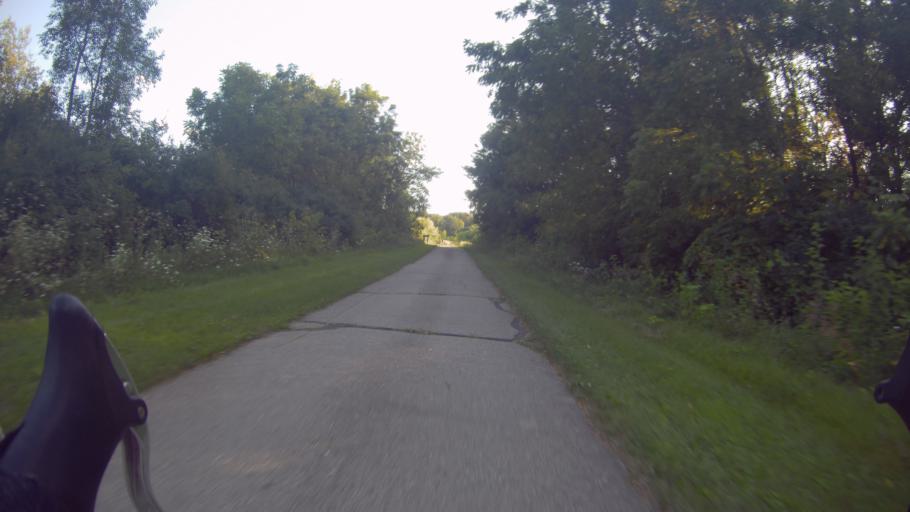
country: US
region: Wisconsin
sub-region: Dane County
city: Madison
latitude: 43.0115
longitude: -89.4106
